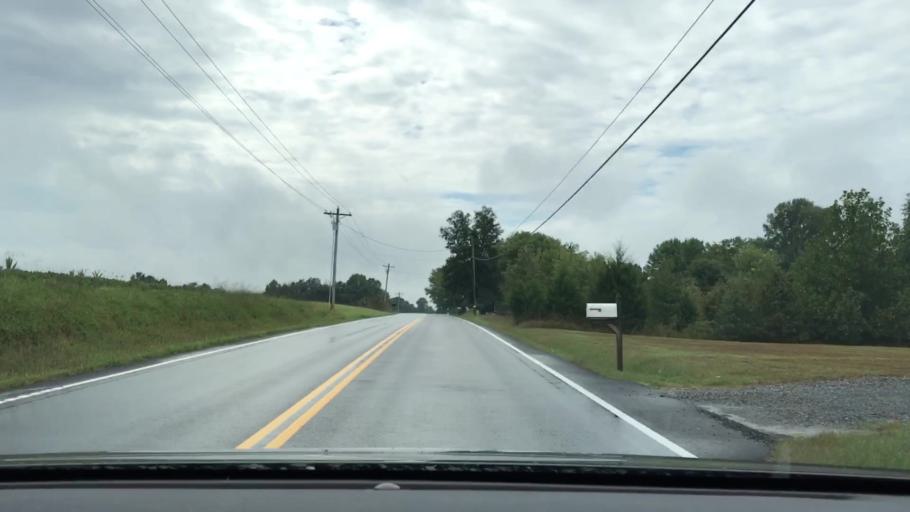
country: US
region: Tennessee
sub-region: Macon County
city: Red Boiling Springs
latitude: 36.4908
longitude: -85.8698
